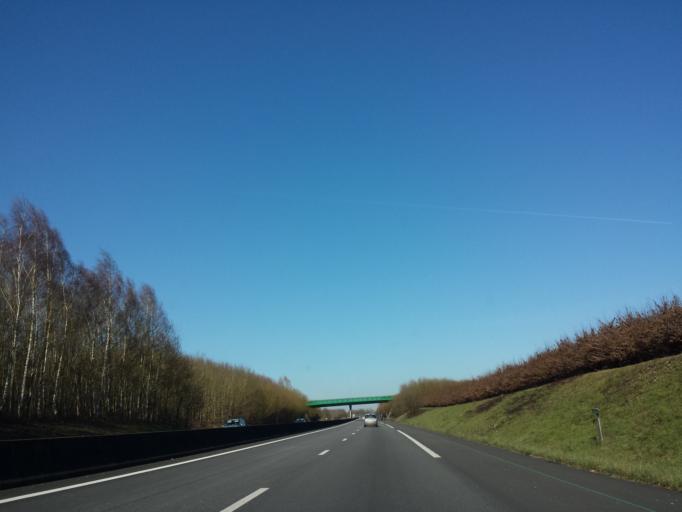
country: FR
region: Picardie
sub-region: Departement de l'Oise
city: Saint-Crepin-Ibouvillers
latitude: 49.2755
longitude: 2.0862
